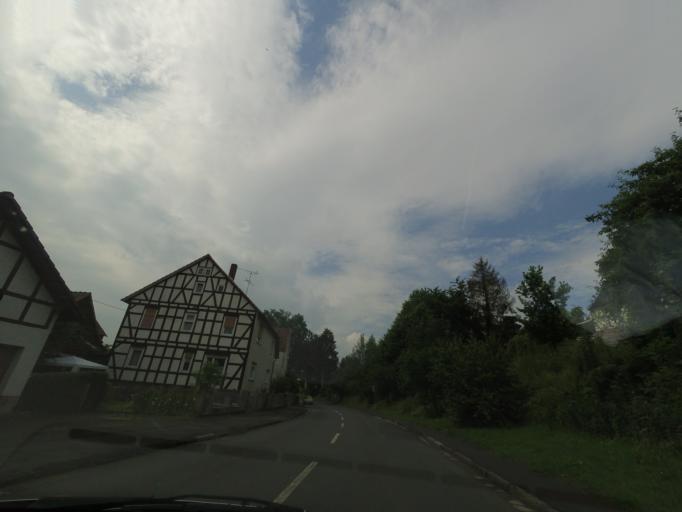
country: DE
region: Hesse
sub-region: Regierungsbezirk Giessen
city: Fronhausen
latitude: 50.7372
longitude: 8.7038
